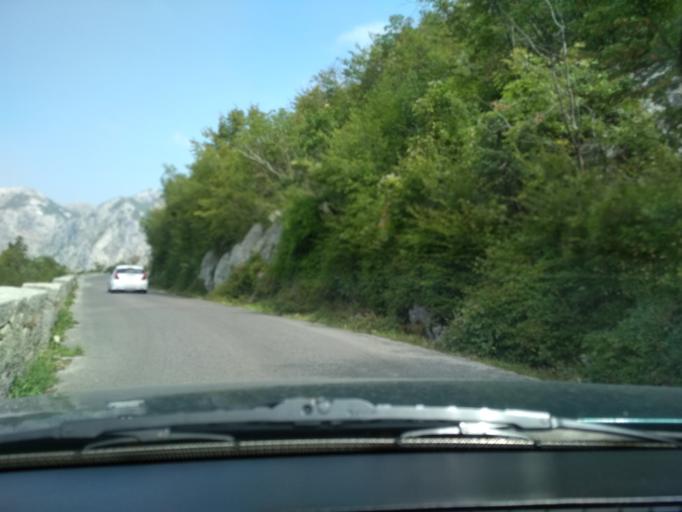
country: ME
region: Kotor
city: Kotor
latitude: 42.4098
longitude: 18.7896
